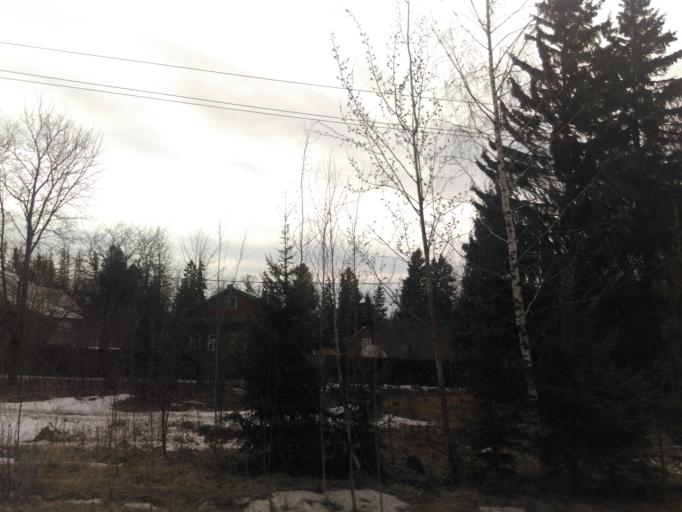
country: RU
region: Moskovskaya
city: Tuchkovo
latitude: 55.6042
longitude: 36.4301
